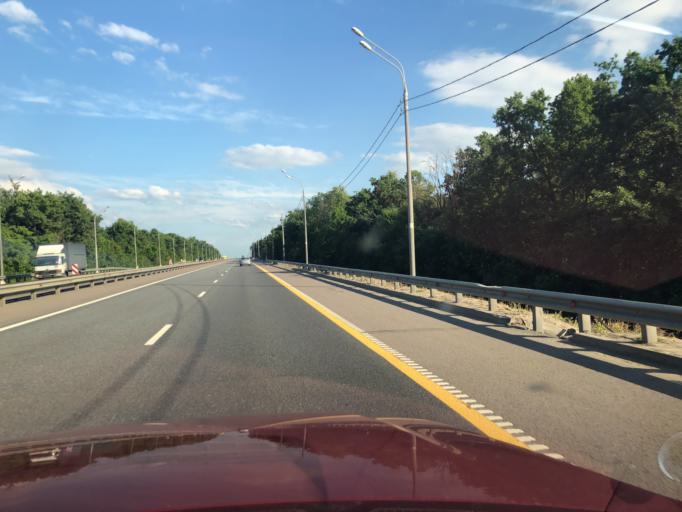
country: RU
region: Lipetsk
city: Zadonsk
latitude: 52.4186
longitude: 38.8388
